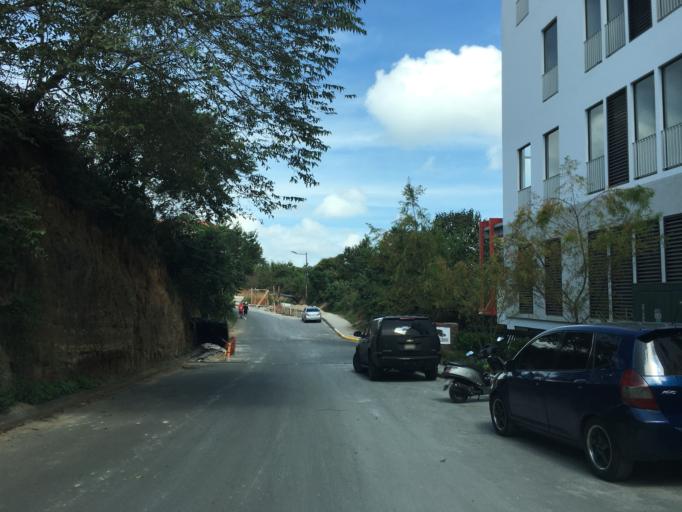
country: GT
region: Guatemala
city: Santa Catarina Pinula
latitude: 14.6067
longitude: -90.4839
